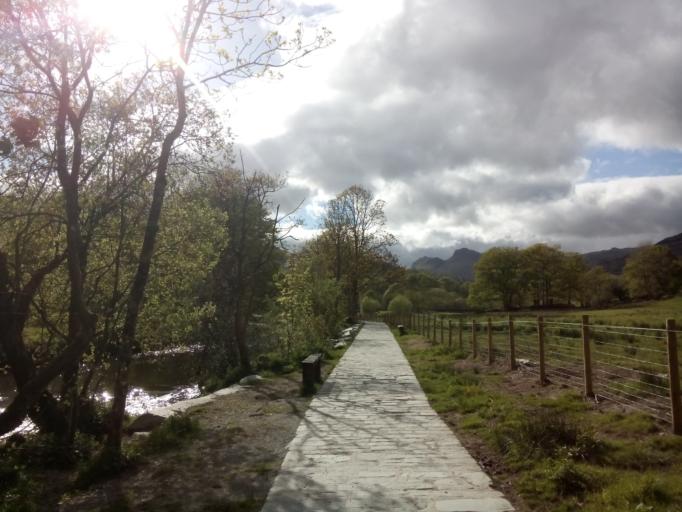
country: GB
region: England
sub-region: Cumbria
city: Ambleside
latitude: 54.4301
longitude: -3.0280
